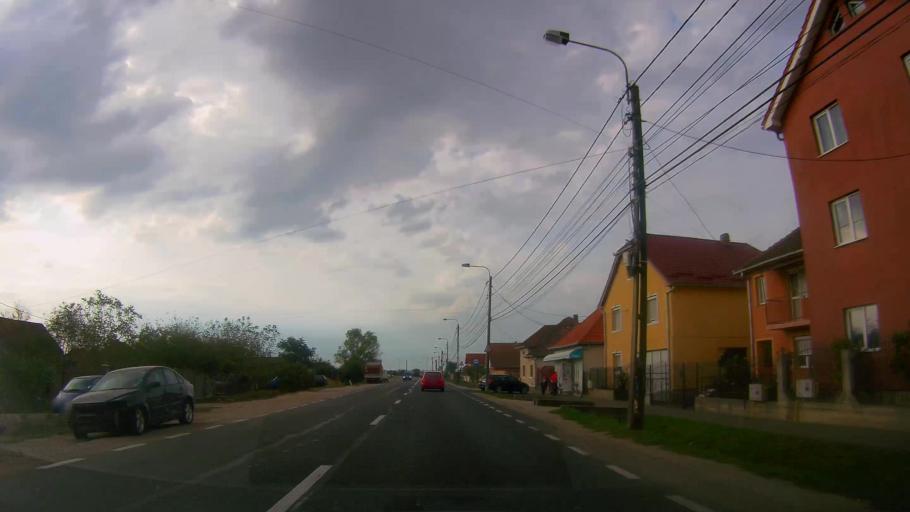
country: RO
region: Satu Mare
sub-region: Oras Ardud
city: Madaras
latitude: 47.7317
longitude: 22.8824
